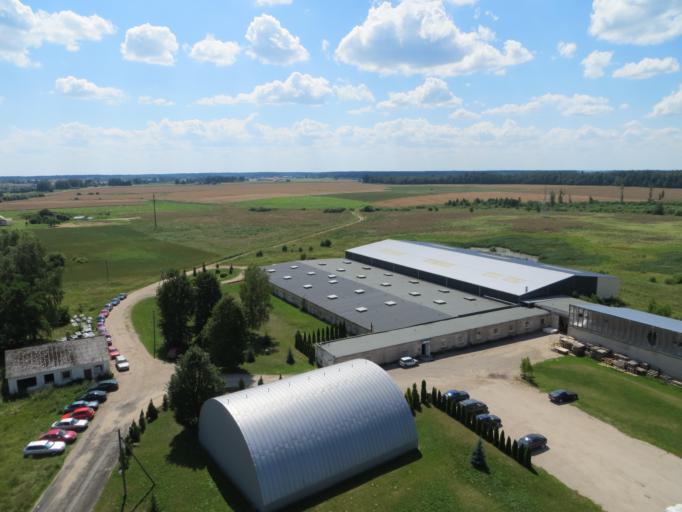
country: LT
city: Sirvintos
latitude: 55.0141
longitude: 24.9805
